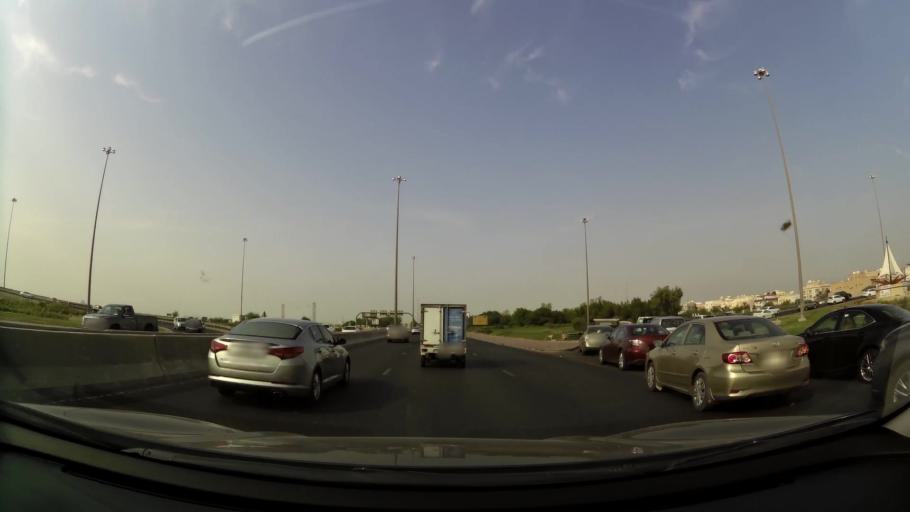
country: KW
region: Al Farwaniyah
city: Al Farwaniyah
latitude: 29.3035
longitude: 47.9635
